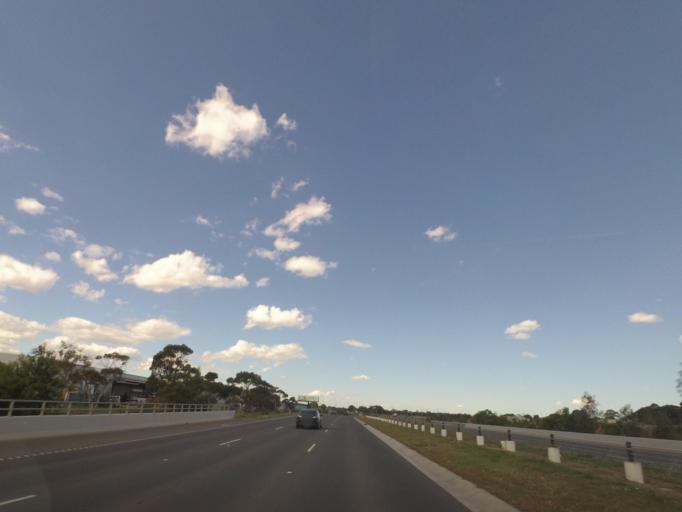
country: AU
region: Victoria
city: Heatherton
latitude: -37.9607
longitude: 145.1228
